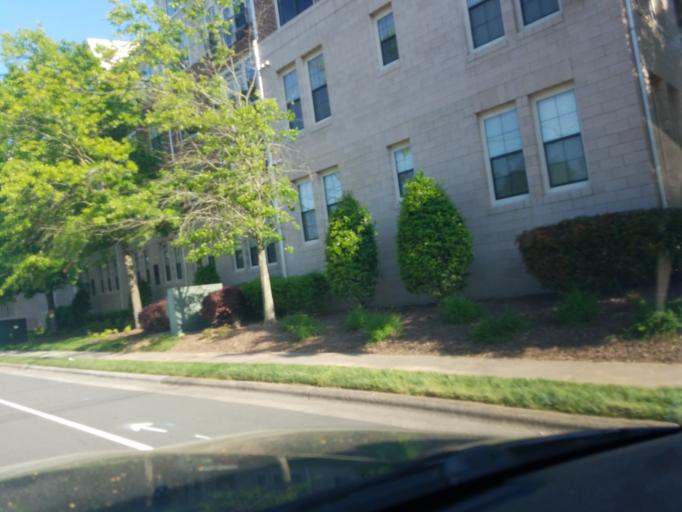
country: US
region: North Carolina
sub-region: Durham County
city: Durham
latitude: 36.0104
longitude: -78.9261
